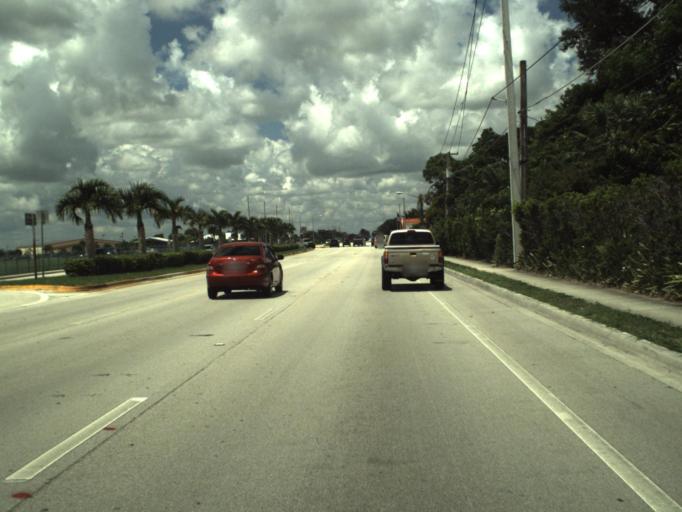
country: US
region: Florida
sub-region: Broward County
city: Pembroke Pines
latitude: 26.0095
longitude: -80.2382
